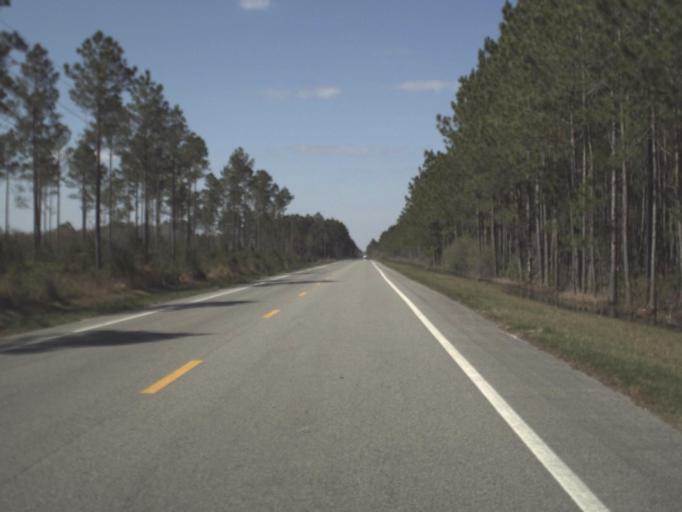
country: US
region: Florida
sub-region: Gulf County
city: Wewahitchka
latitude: 30.0051
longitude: -85.1738
